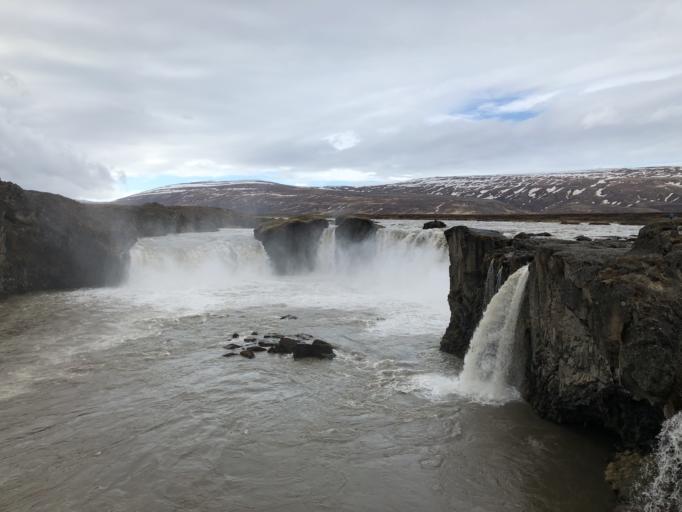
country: IS
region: Northeast
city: Laugar
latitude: 65.6837
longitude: -17.5494
